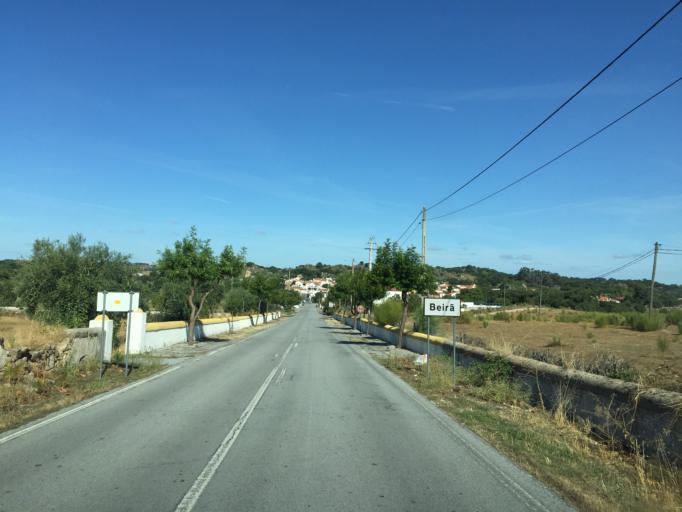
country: PT
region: Portalegre
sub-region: Marvao
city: Marvao
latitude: 39.4424
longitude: -7.3675
